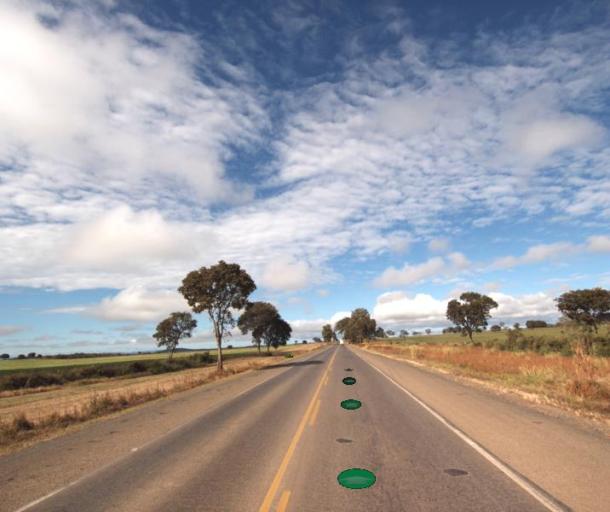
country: BR
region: Goias
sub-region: Uruacu
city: Uruacu
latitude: -14.6789
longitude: -49.2048
